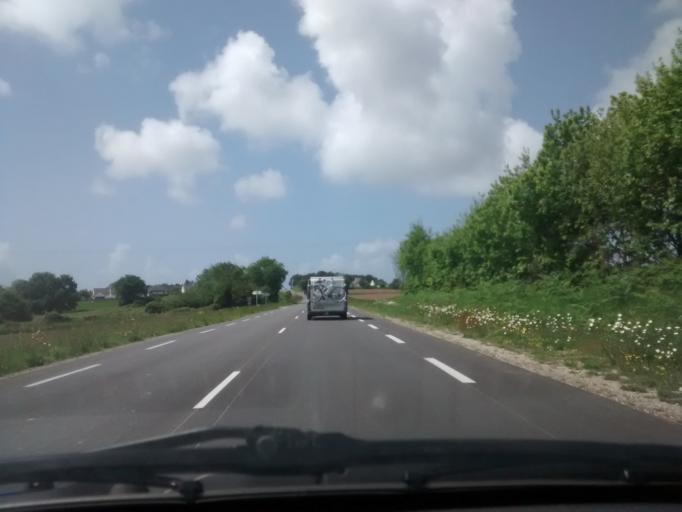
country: FR
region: Brittany
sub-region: Departement du Morbihan
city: Larmor-Baden
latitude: 47.6169
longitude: -2.8775
